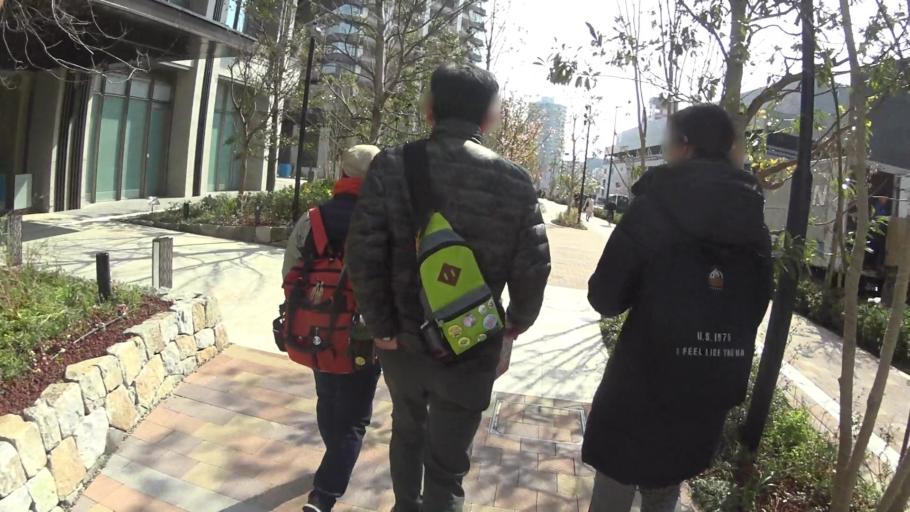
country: JP
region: Tokyo
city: Tokyo
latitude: 35.6327
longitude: 139.7162
